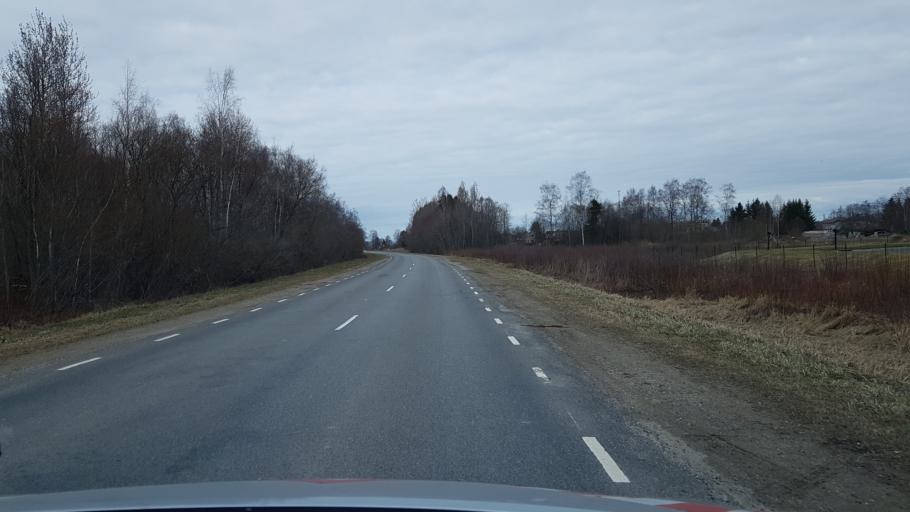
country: EE
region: Ida-Virumaa
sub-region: Sillamaee linn
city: Sillamae
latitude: 59.3655
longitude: 27.7592
